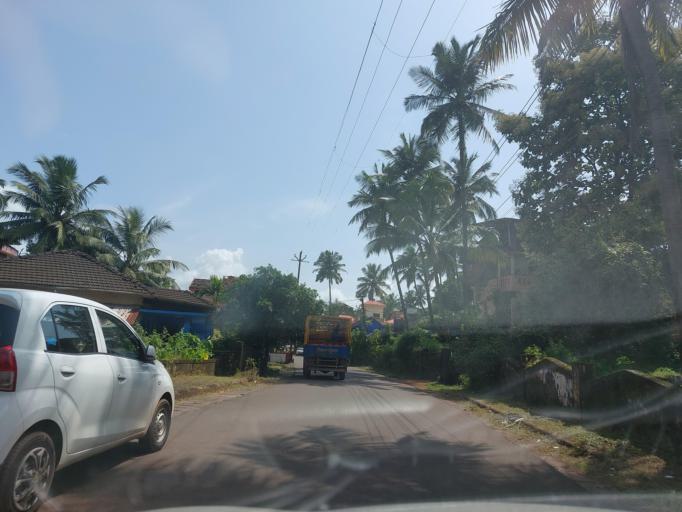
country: IN
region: Goa
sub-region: North Goa
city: Ponda
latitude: 15.3995
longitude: 74.0018
